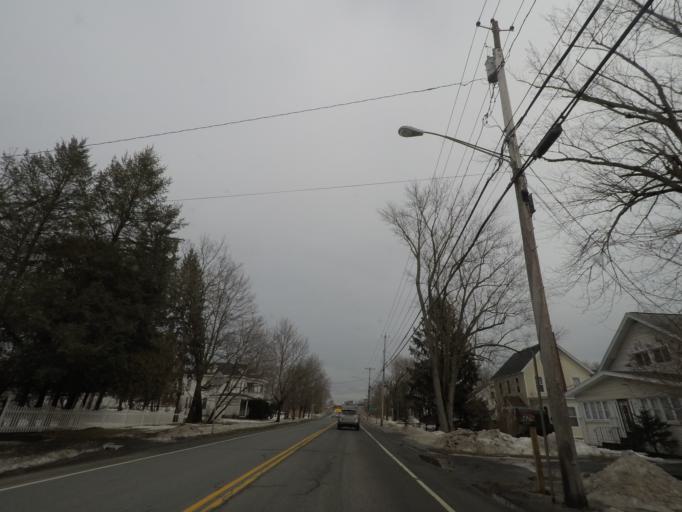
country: US
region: New York
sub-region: Albany County
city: Voorheesville
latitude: 42.7023
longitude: -73.9612
